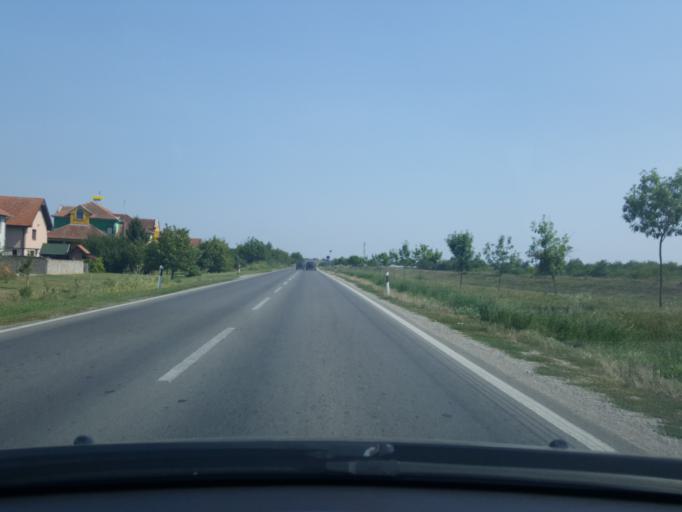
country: RS
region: Central Serbia
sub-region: Macvanski Okrug
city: Sabac
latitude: 44.7460
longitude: 19.6667
